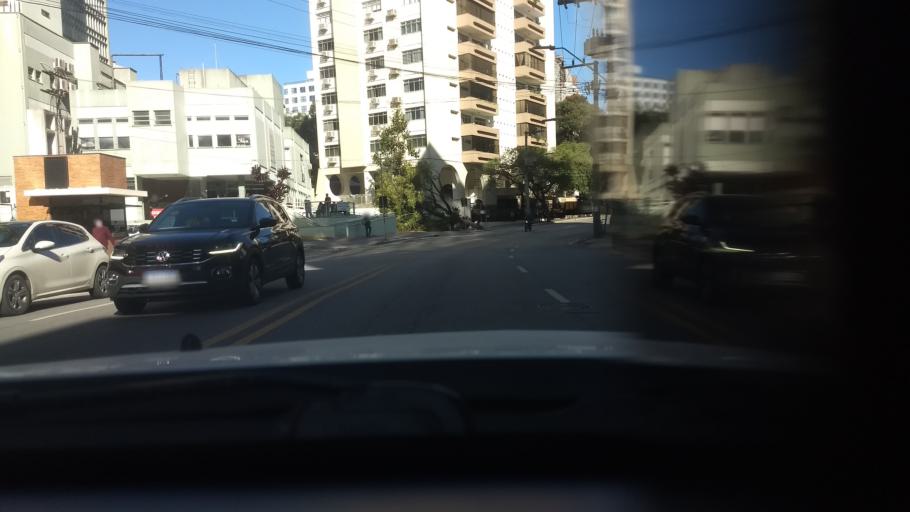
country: BR
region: Santa Catarina
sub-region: Florianopolis
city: Florianopolis
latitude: -27.5877
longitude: -48.5514
